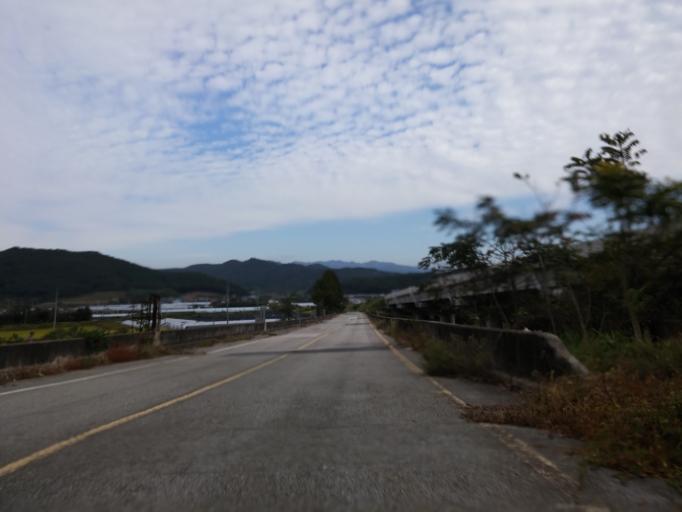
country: KR
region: Chungcheongnam-do
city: Yonmu
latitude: 36.1629
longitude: 127.1978
